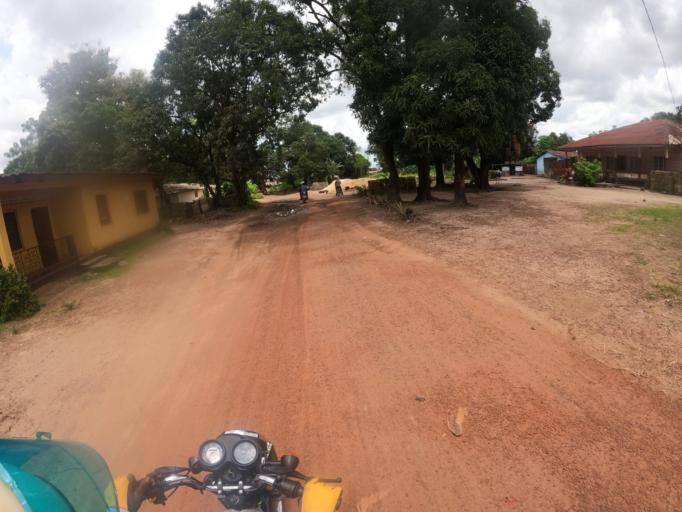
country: SL
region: Northern Province
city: Makeni
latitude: 8.8913
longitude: -12.0557
